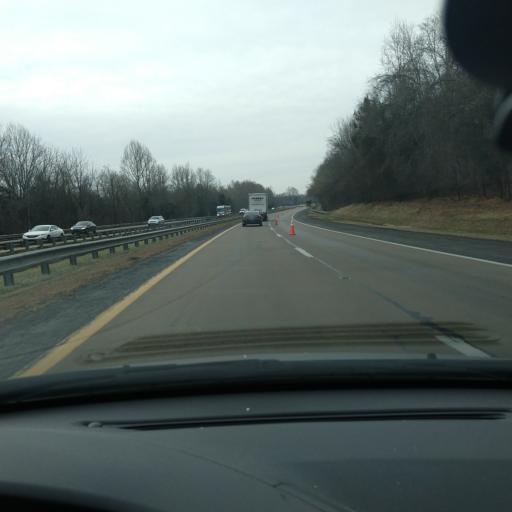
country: US
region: North Carolina
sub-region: Forsyth County
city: Winston-Salem
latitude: 36.0283
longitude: -80.2366
